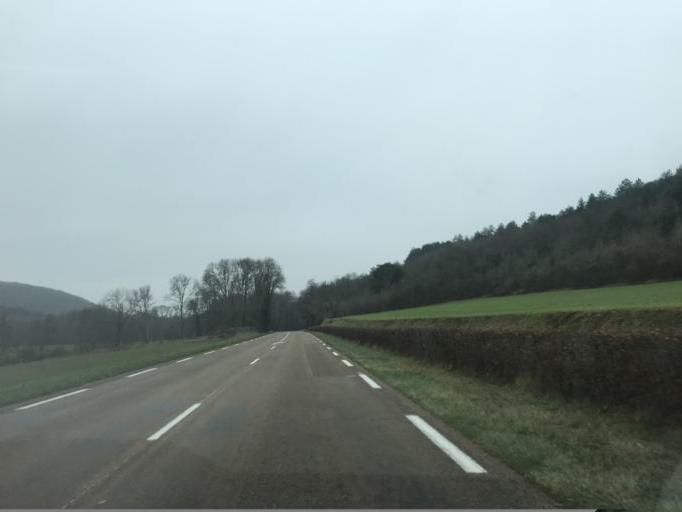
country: FR
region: Bourgogne
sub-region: Departement de l'Yonne
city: Avallon
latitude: 47.5222
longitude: 3.7761
